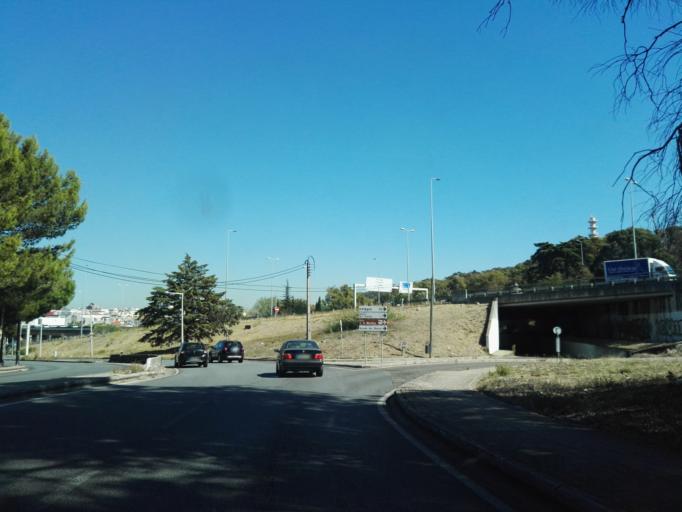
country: PT
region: Lisbon
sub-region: Odivelas
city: Pontinha
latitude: 38.7421
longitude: -9.1998
